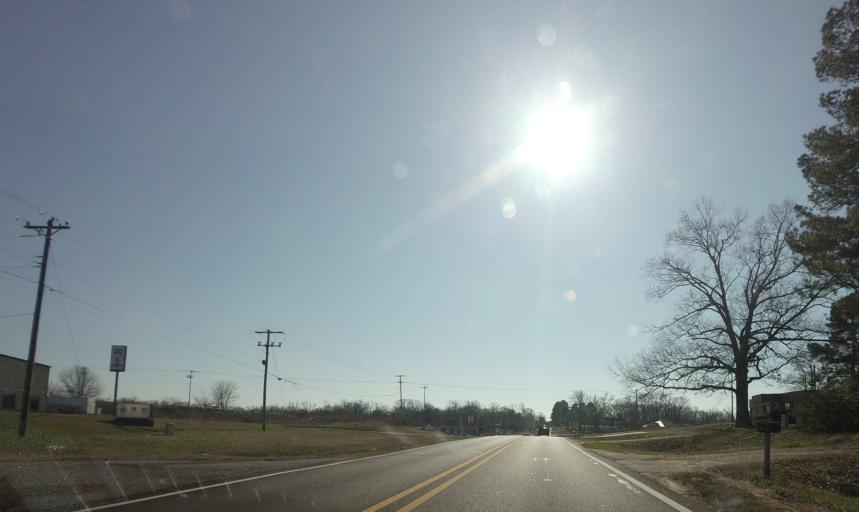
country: US
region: Tennessee
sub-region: Shelby County
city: Collierville
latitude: 34.9648
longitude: -89.6890
